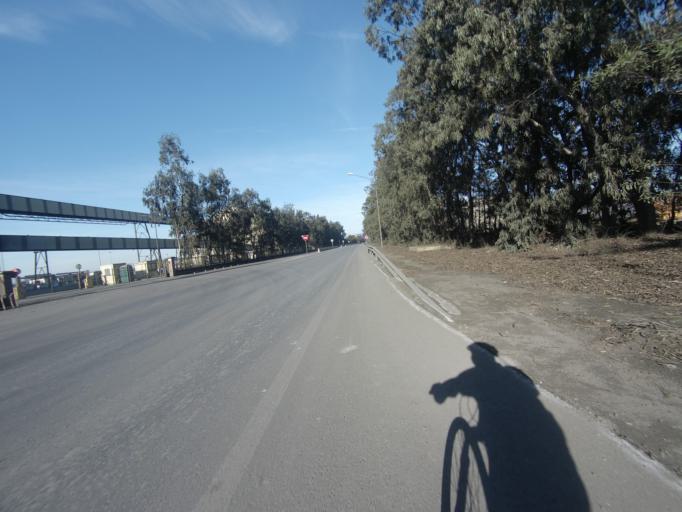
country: ES
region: Andalusia
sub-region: Provincia de Huelva
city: Punta Umbria
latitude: 37.1835
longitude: -6.9240
